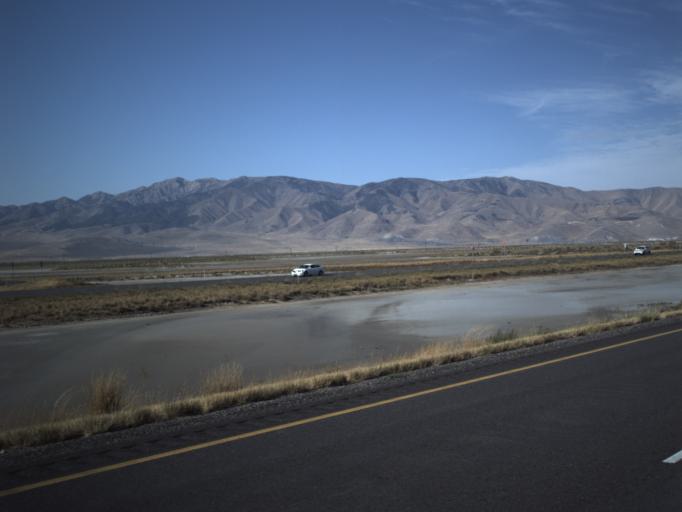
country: US
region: Utah
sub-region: Tooele County
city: Grantsville
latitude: 40.6854
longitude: -112.4454
